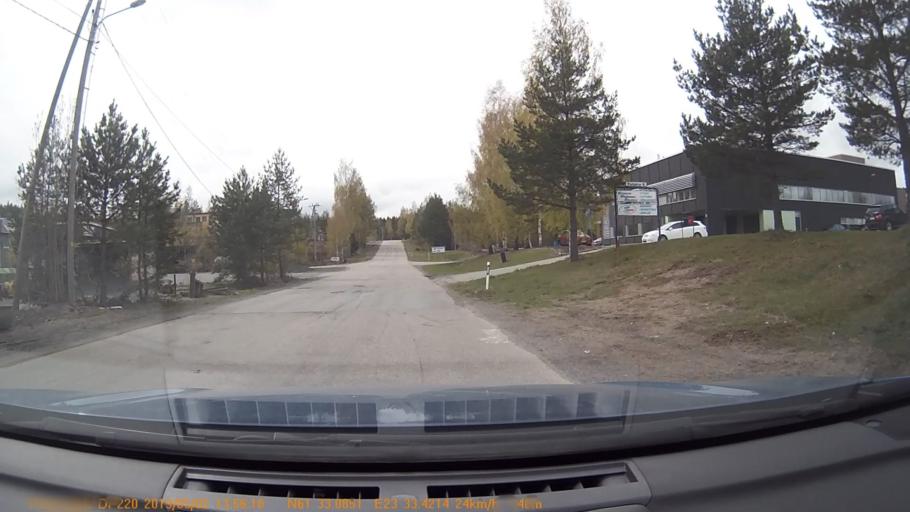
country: FI
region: Pirkanmaa
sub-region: Tampere
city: Yloejaervi
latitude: 61.5514
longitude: 23.5571
